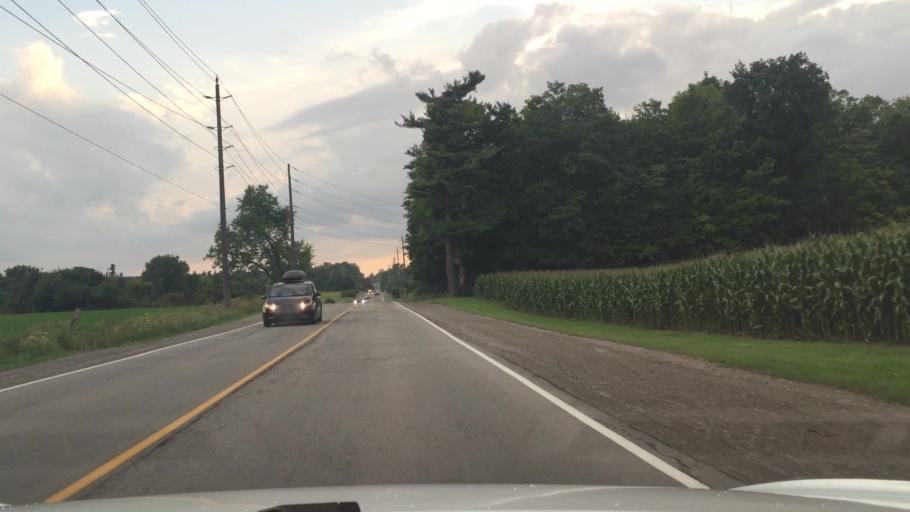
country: CA
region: Ontario
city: Markham
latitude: 43.8444
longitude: -79.2176
